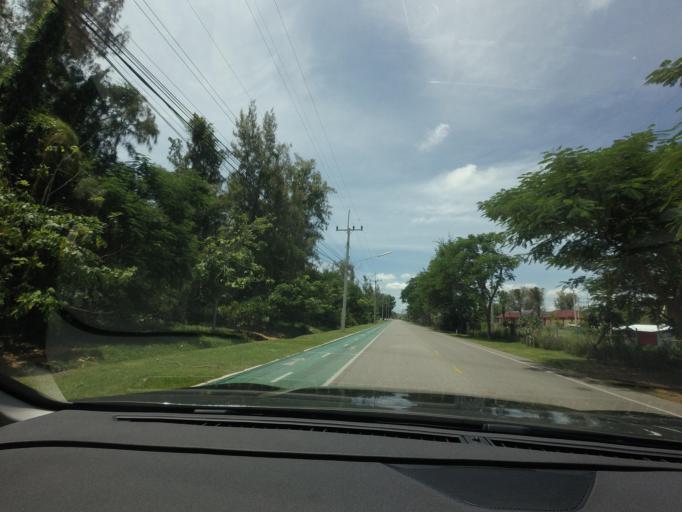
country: TH
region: Prachuap Khiri Khan
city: Hua Hin
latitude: 12.5013
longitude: 99.9728
